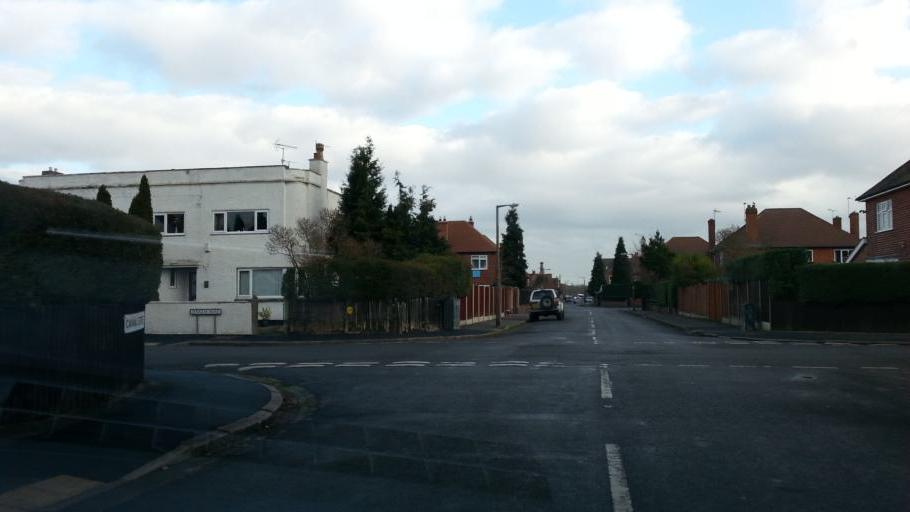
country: GB
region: England
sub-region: Derbyshire
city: Long Eaton
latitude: 52.9036
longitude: -1.2885
